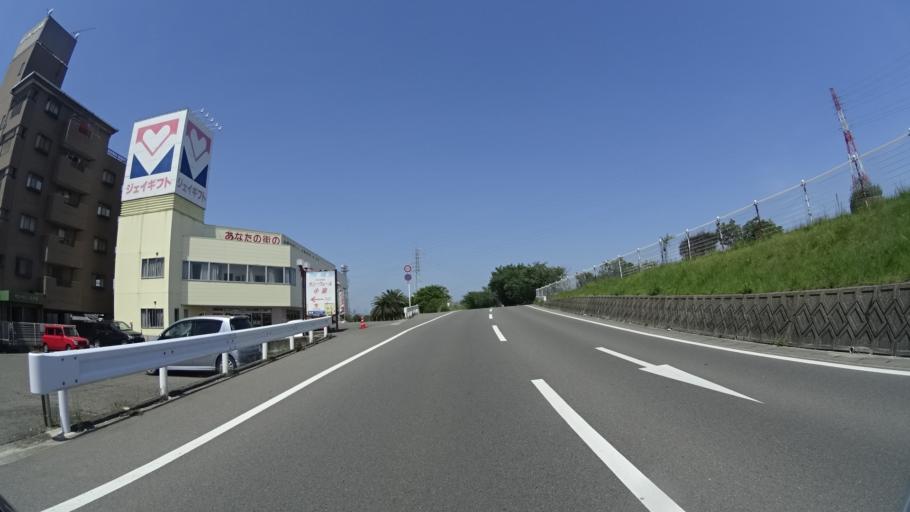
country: JP
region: Ehime
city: Hojo
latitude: 34.0470
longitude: 132.9854
